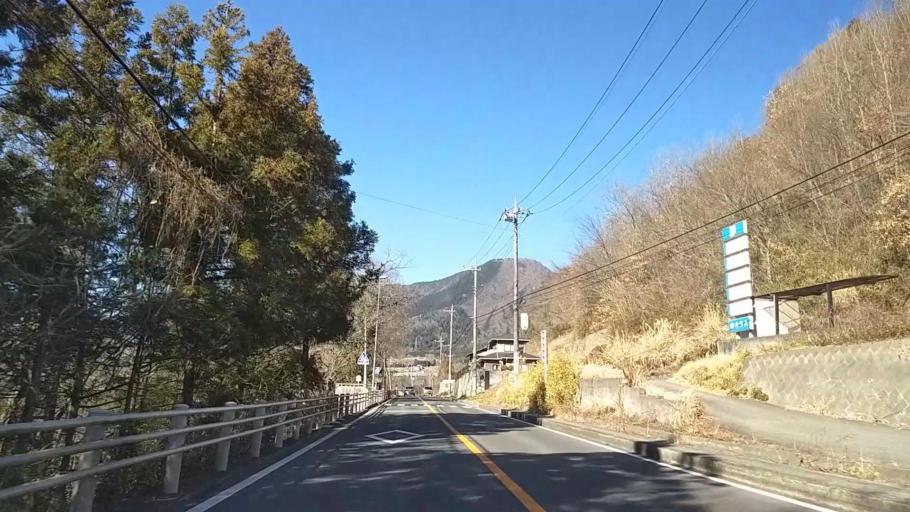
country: JP
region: Yamanashi
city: Otsuki
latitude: 35.6113
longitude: 138.9955
